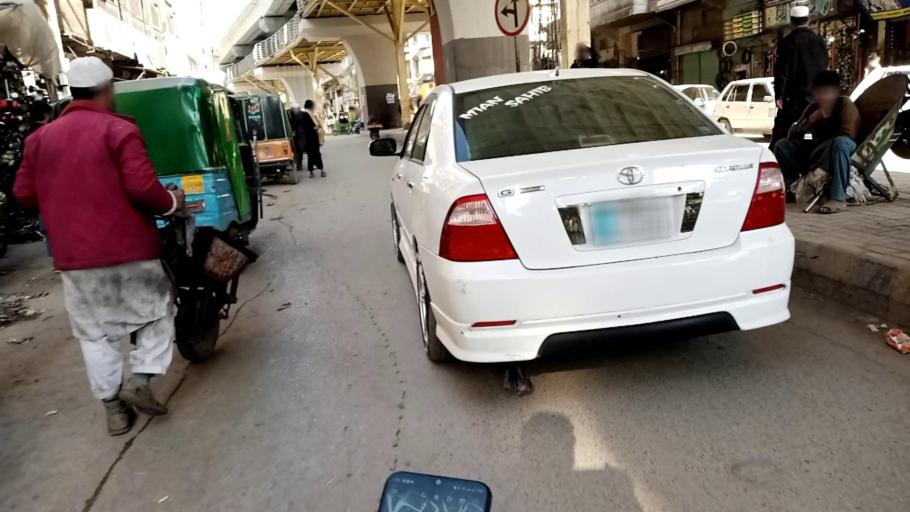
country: PK
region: Khyber Pakhtunkhwa
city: Peshawar
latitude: 34.0085
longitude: 71.5627
